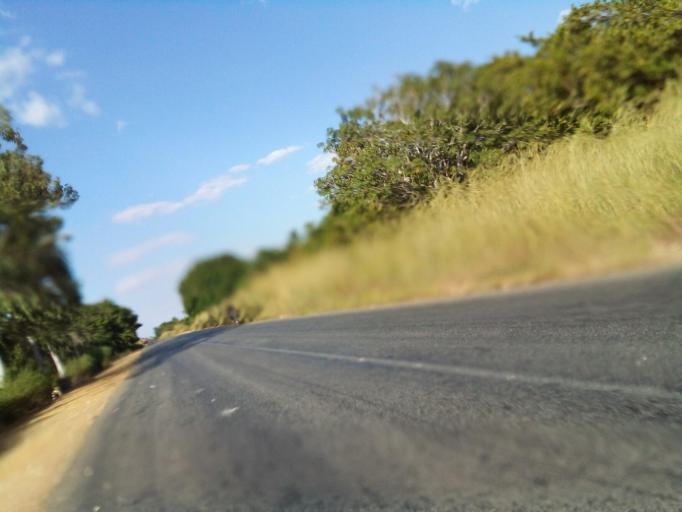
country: MZ
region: Zambezia
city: Quelimane
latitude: -17.5752
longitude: 36.6238
